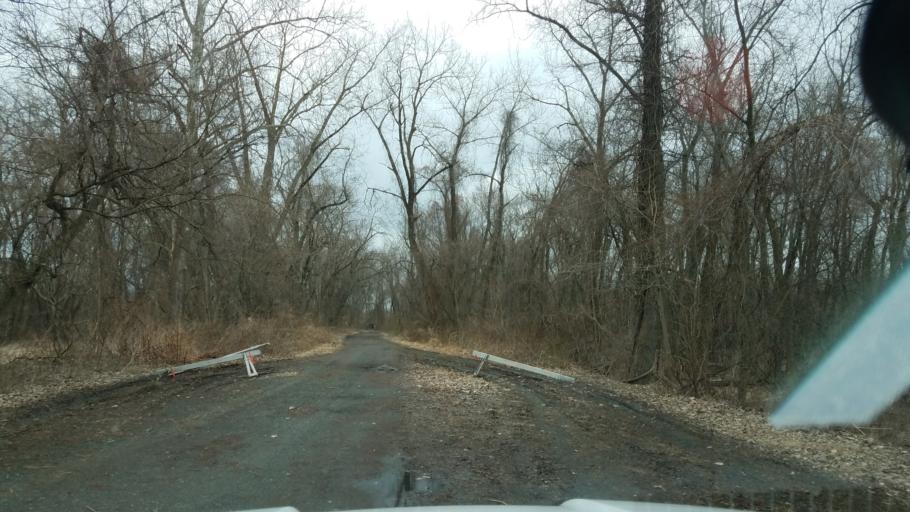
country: US
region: Connecticut
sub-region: Hartford County
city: Wethersfield
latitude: 41.7107
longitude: -72.6338
